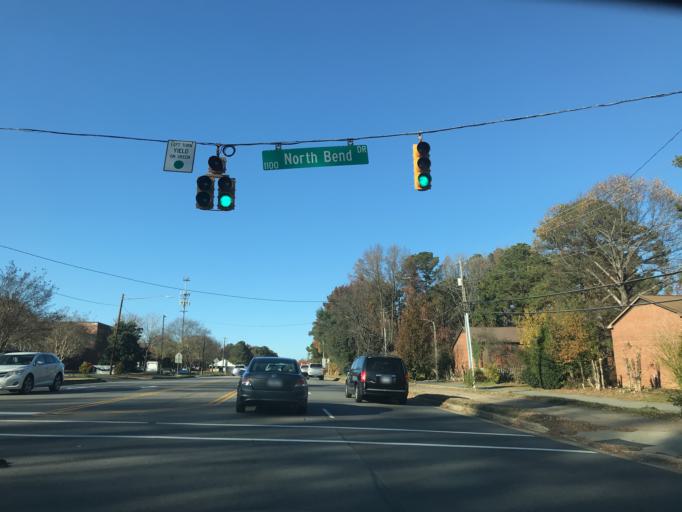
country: US
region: North Carolina
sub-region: Wake County
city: West Raleigh
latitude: 35.8614
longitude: -78.6191
